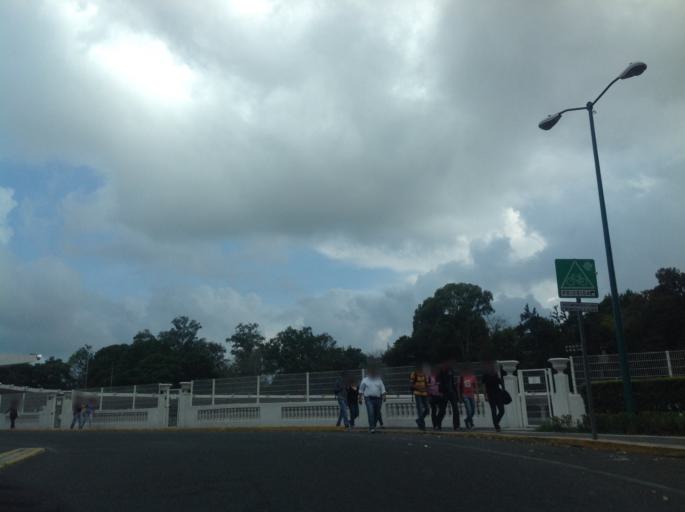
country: MX
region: Veracruz
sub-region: Xalapa
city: Xalapa de Enriquez
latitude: 19.5206
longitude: -96.9186
